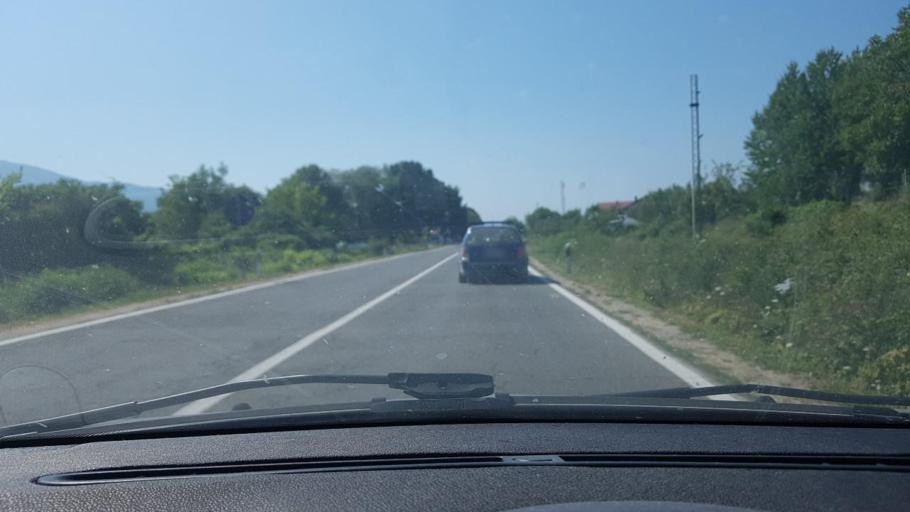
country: BA
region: Federation of Bosnia and Herzegovina
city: Bihac
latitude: 44.8003
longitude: 15.9103
